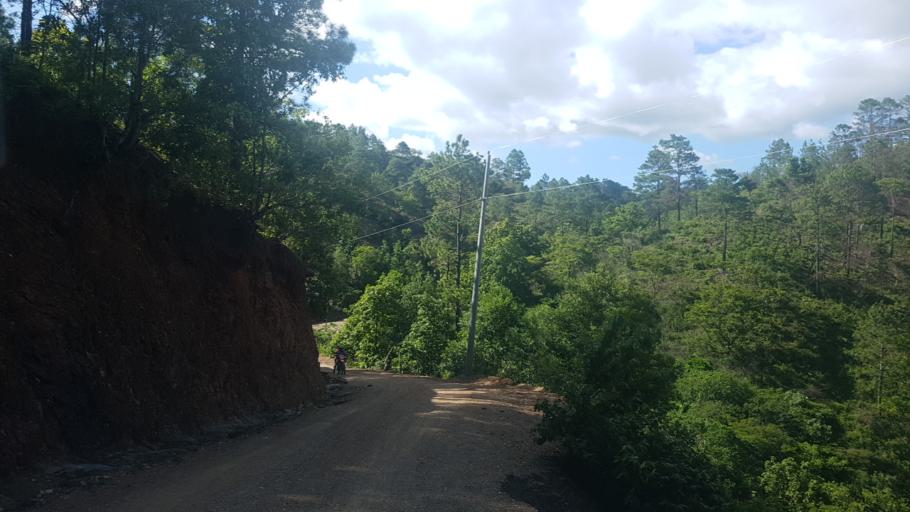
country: HN
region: Choluteca
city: Duyure
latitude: 13.6478
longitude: -86.6553
